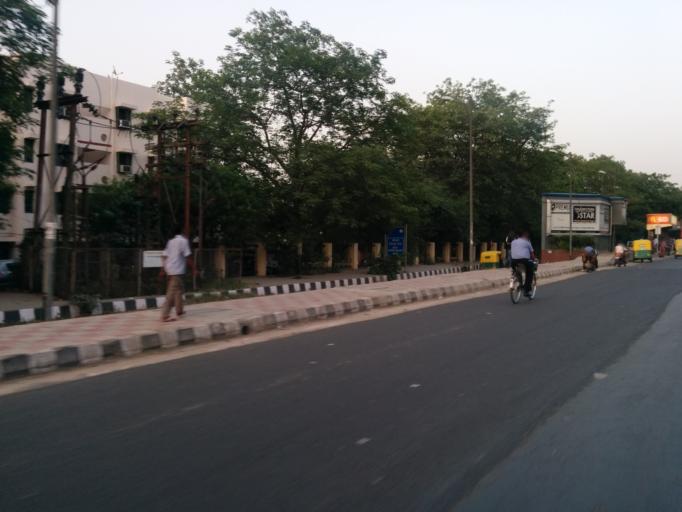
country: IN
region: NCT
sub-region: New Delhi
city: New Delhi
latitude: 28.5698
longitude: 77.2035
